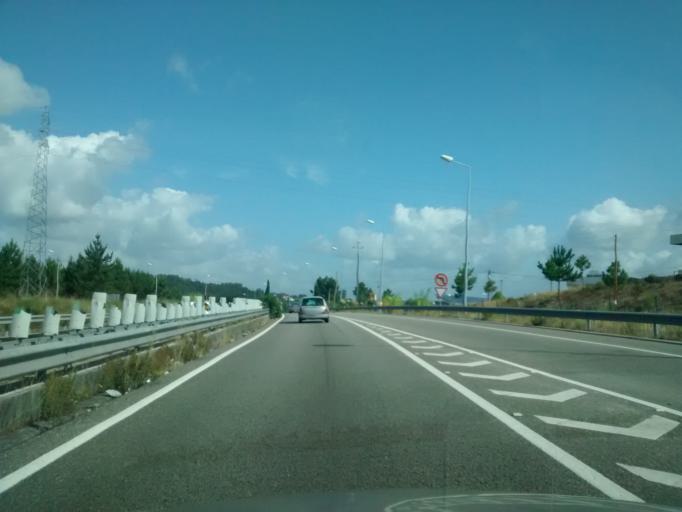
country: PT
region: Aveiro
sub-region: Oliveira do Bairro
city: Oliveira do Bairro
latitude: 40.5237
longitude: -8.5059
